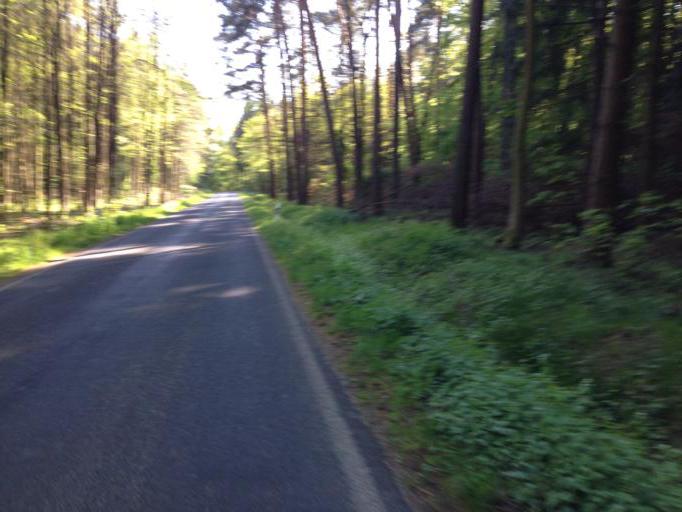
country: DE
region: Hesse
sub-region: Regierungsbezirk Giessen
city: Grossen Buseck
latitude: 50.5675
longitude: 8.7930
